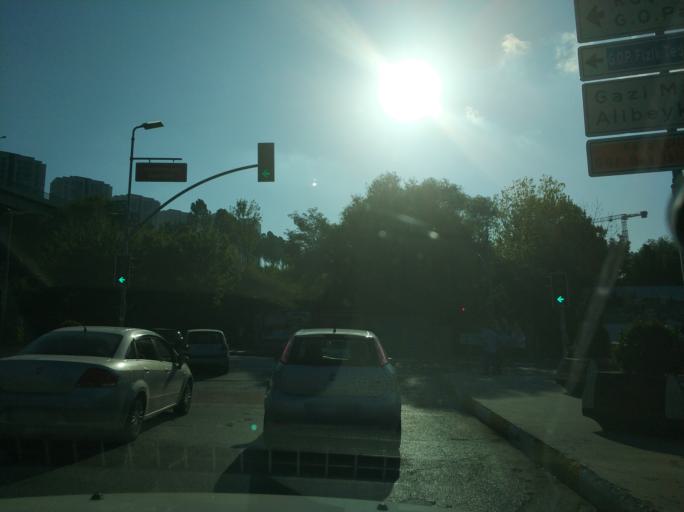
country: TR
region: Istanbul
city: Sultangazi
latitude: 41.0915
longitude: 28.9068
